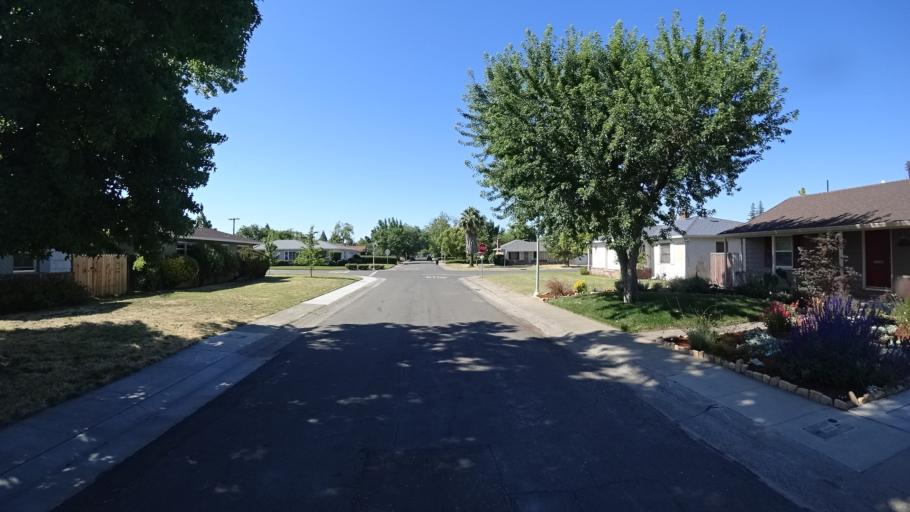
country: US
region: California
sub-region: Sacramento County
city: Parkway
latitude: 38.5287
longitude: -121.4883
